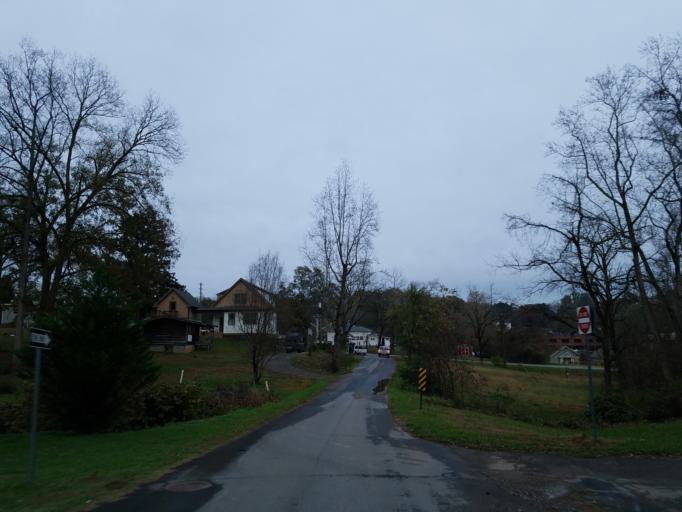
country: US
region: Georgia
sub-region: Cherokee County
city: Ball Ground
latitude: 34.3367
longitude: -84.3802
